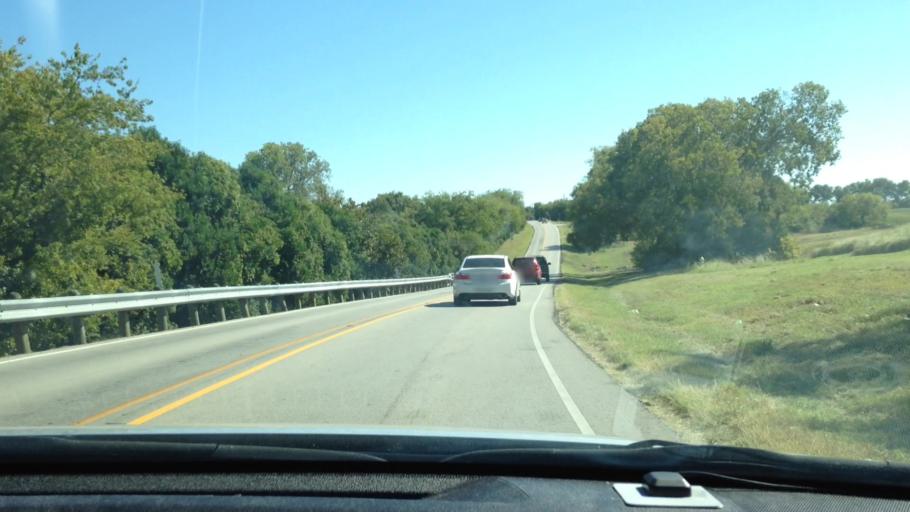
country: US
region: Texas
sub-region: Collin County
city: Lucas
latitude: 33.0741
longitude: -96.5718
